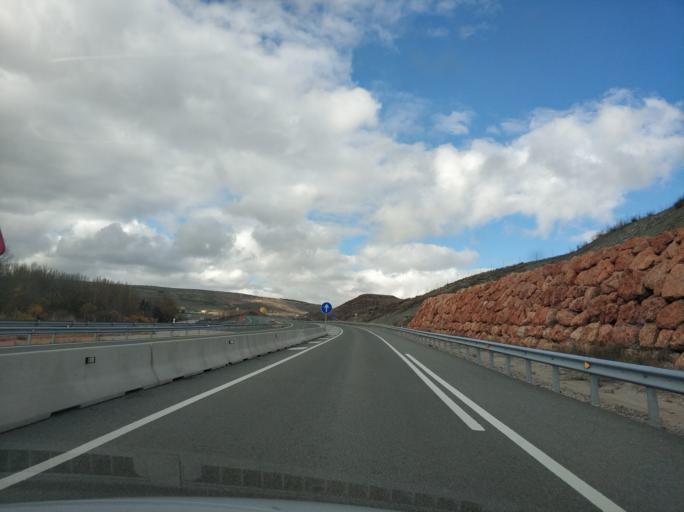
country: ES
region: Castille and Leon
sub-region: Provincia de Soria
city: Medinaceli
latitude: 41.1747
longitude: -2.4222
